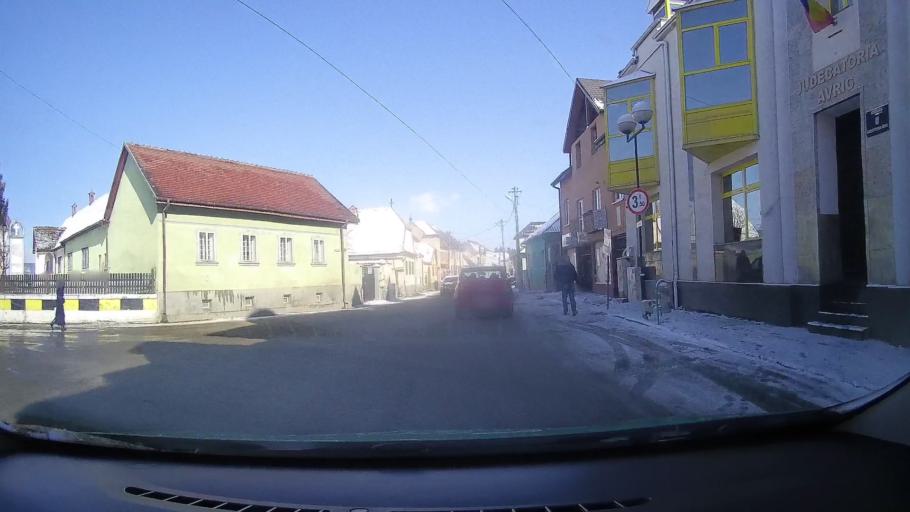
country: RO
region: Sibiu
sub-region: Comuna Avrig
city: Avrig
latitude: 45.7262
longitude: 24.3749
